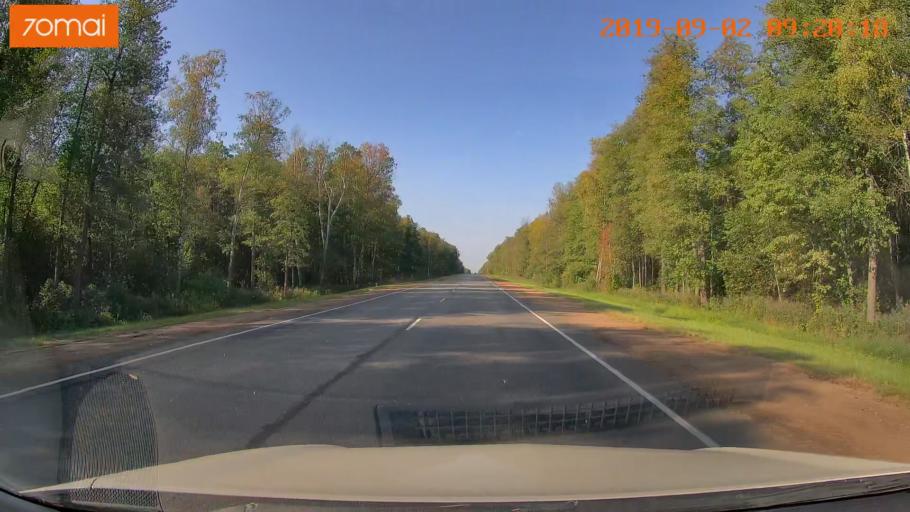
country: RU
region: Kaluga
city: Yukhnov
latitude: 54.8015
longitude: 35.3868
